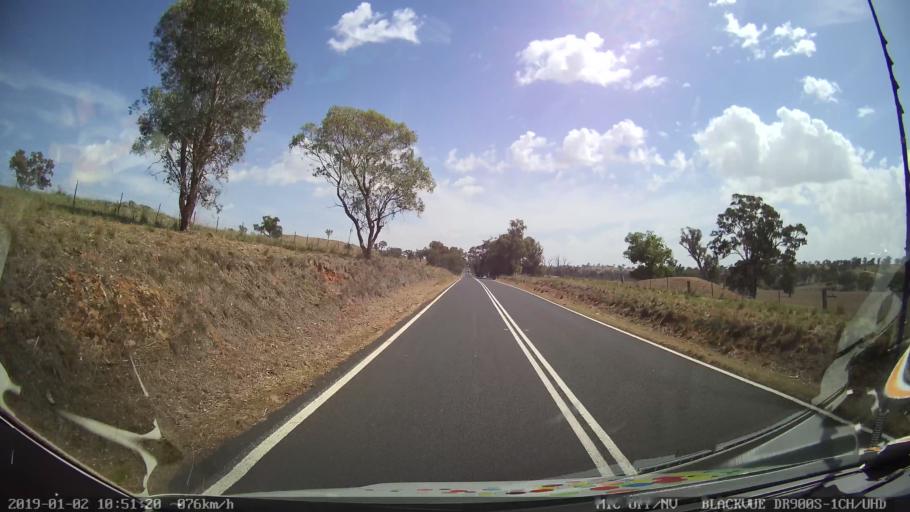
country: AU
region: New South Wales
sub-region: Cootamundra
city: Cootamundra
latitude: -34.7013
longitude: 148.2758
